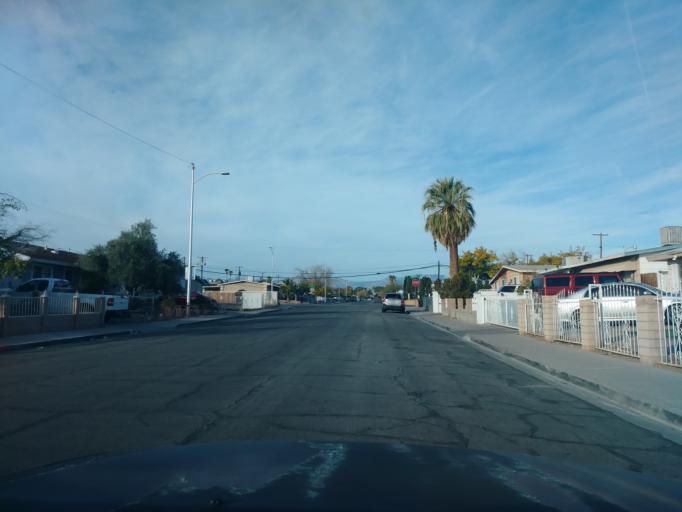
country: US
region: Nevada
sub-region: Clark County
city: Spring Valley
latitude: 36.1616
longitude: -115.2323
